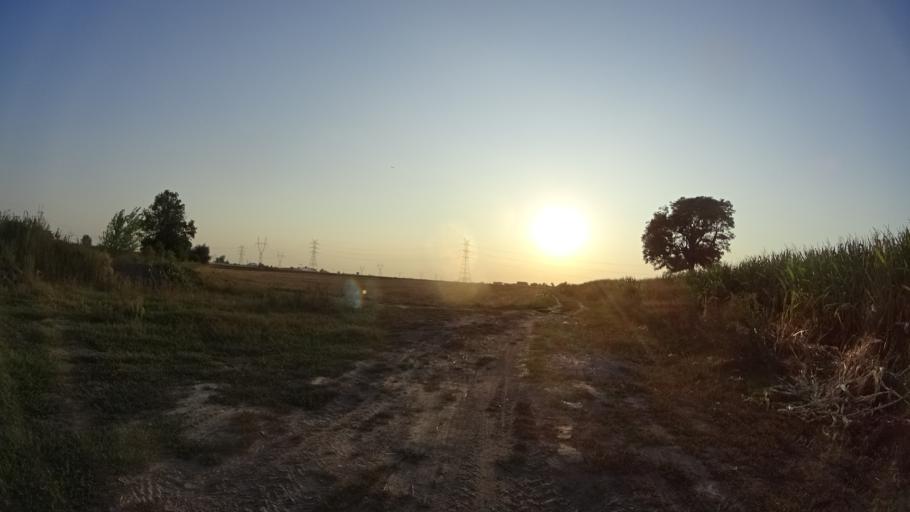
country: PL
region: Masovian Voivodeship
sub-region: Powiat warszawski zachodni
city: Ozarow Mazowiecki
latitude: 52.2404
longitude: 20.7760
